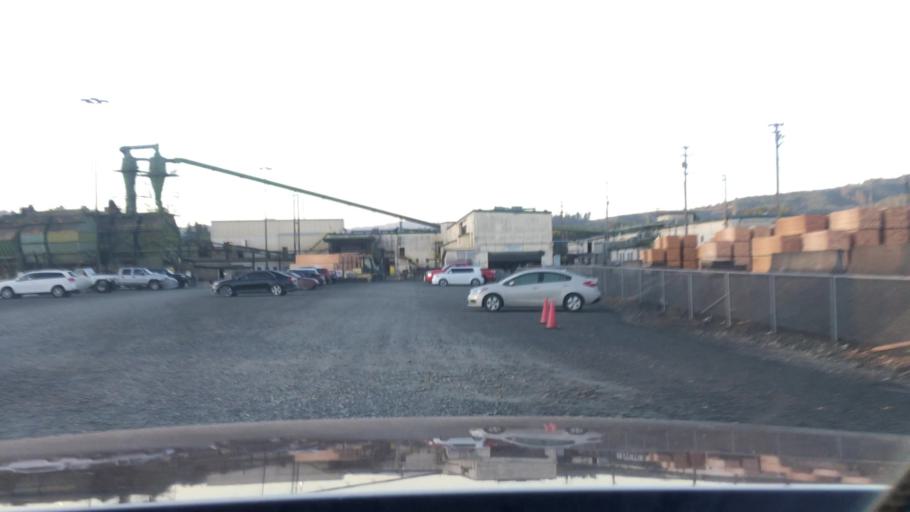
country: US
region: Oregon
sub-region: Lane County
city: Cottage Grove
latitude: 43.7679
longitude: -123.0784
